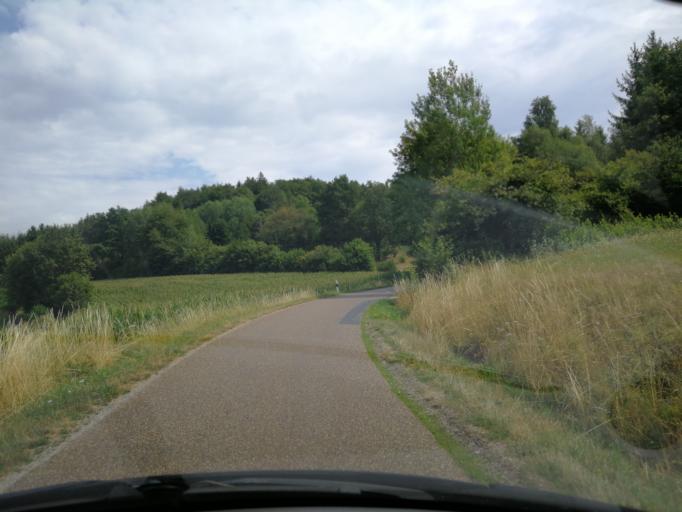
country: DE
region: Bavaria
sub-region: Upper Palatinate
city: Brennberg
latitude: 49.0707
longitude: 12.4096
